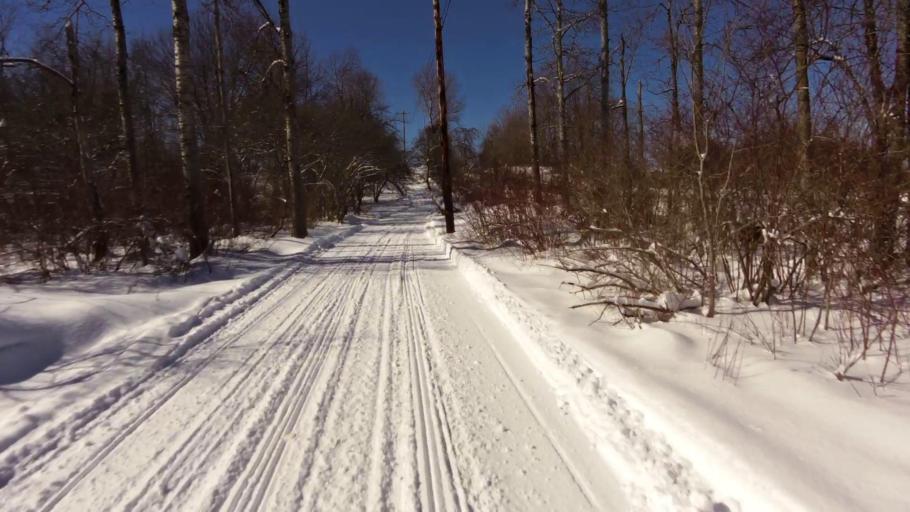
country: US
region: New York
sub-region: Chautauqua County
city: Mayville
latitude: 42.2278
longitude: -79.4132
